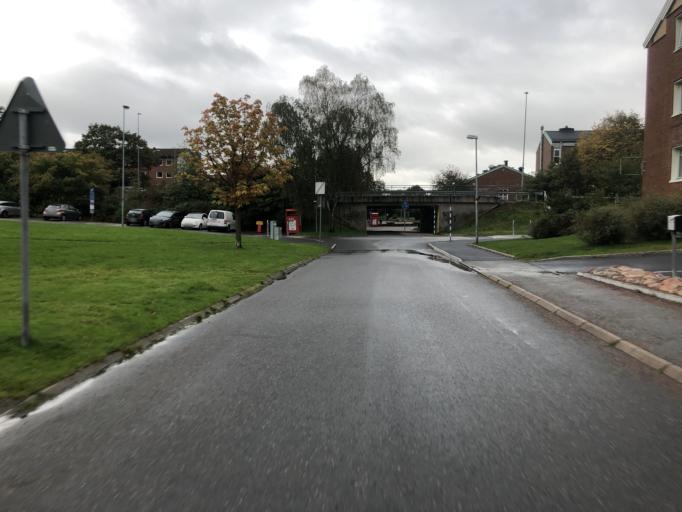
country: SE
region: Vaestra Goetaland
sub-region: Molndal
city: Moelndal
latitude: 57.6600
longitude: 12.0029
